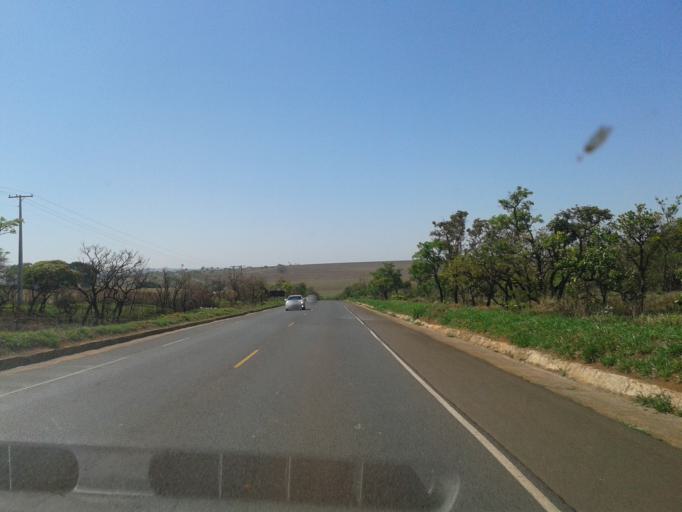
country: BR
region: Minas Gerais
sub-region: Uberlandia
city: Uberlandia
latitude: -19.1057
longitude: -47.9829
